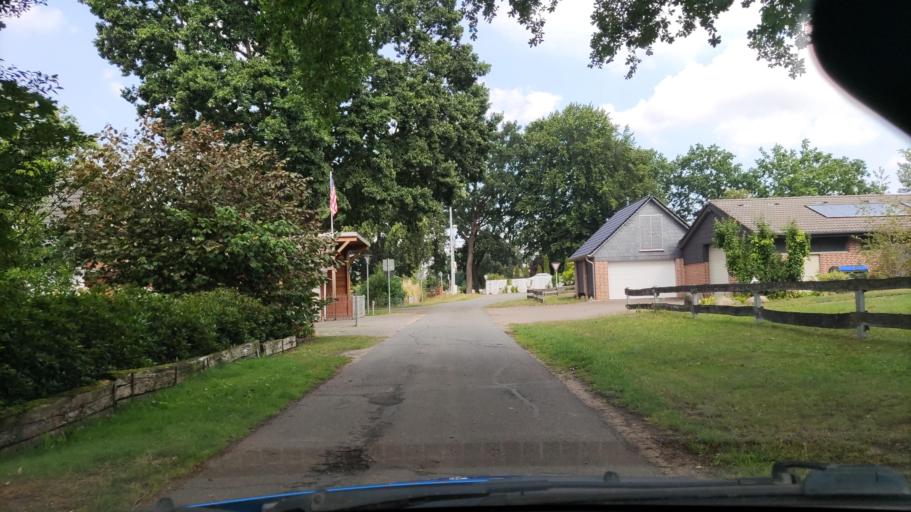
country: DE
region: Lower Saxony
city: Barum
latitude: 53.3474
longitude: 10.4151
